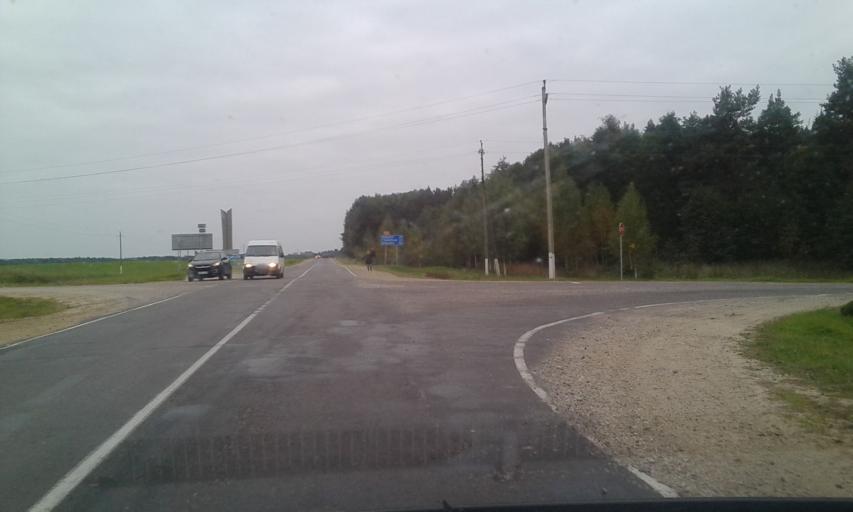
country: BY
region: Vitebsk
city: Pastavy
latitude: 55.1027
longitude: 26.8751
